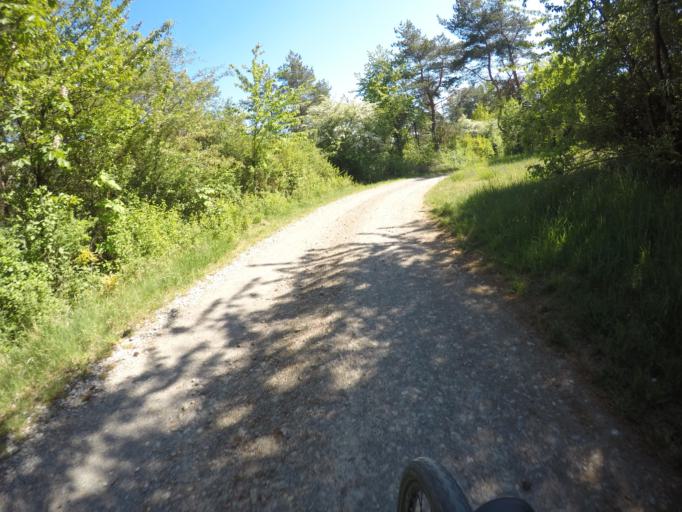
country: DE
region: Baden-Wuerttemberg
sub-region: Regierungsbezirk Stuttgart
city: Weissach
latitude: 48.8324
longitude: 8.8999
